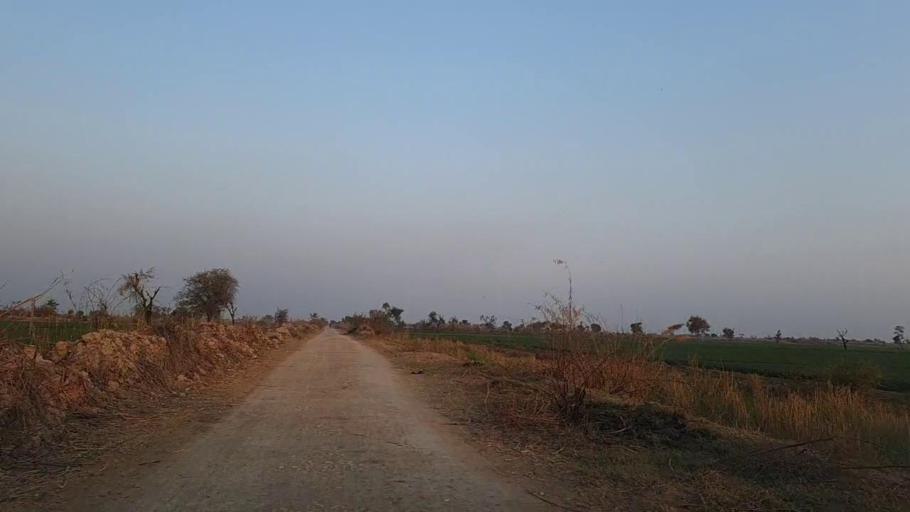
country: PK
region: Sindh
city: Jam Sahib
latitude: 26.3051
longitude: 68.5553
